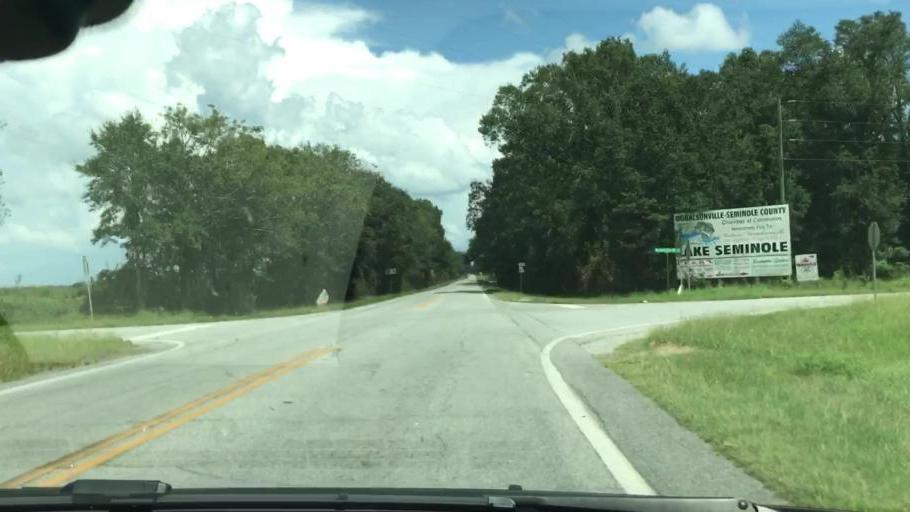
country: US
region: Georgia
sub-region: Seminole County
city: Donalsonville
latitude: 30.9822
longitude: -84.9754
